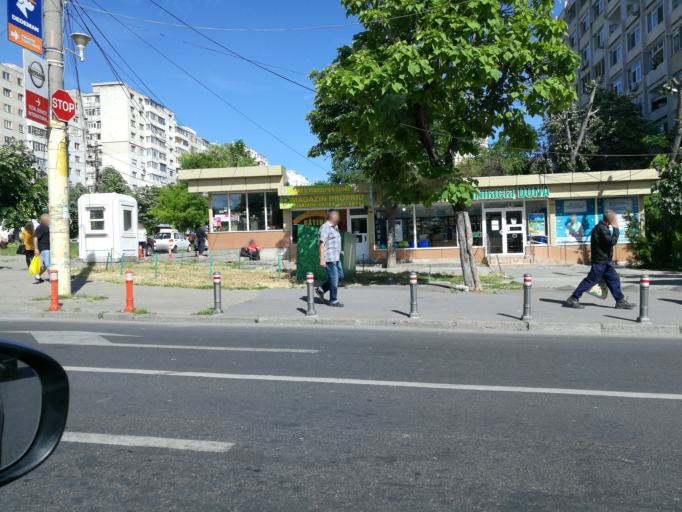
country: RO
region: Constanta
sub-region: Municipiul Constanta
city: Constanta
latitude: 44.2007
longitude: 28.6269
